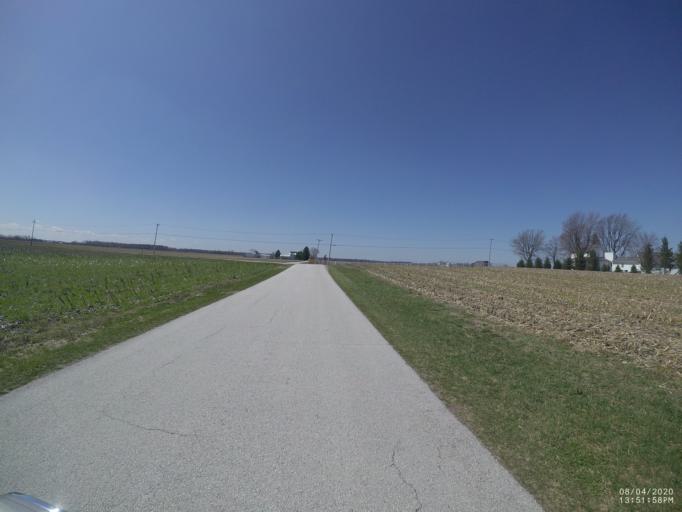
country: US
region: Ohio
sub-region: Sandusky County
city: Gibsonburg
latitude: 41.3272
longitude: -83.3048
